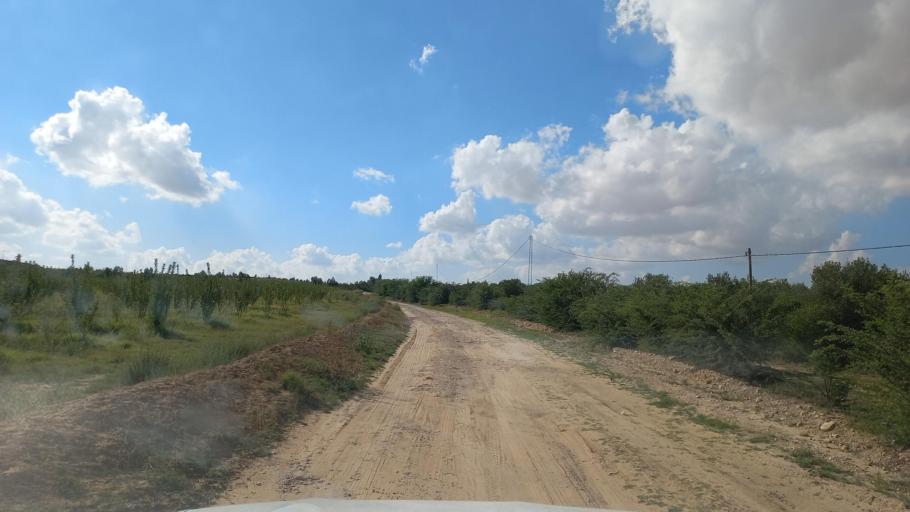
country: TN
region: Al Qasrayn
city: Sbiba
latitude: 35.3354
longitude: 9.0858
